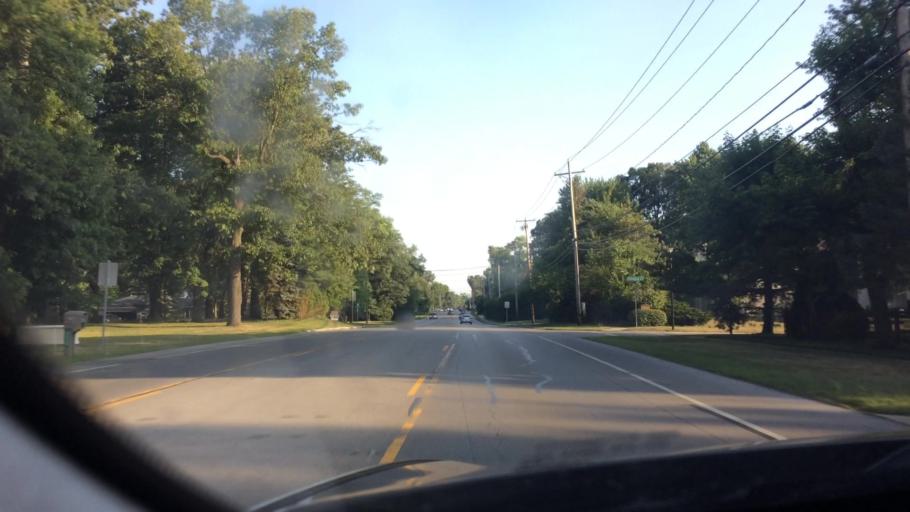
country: US
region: Ohio
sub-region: Lucas County
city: Holland
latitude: 41.6687
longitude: -83.7028
